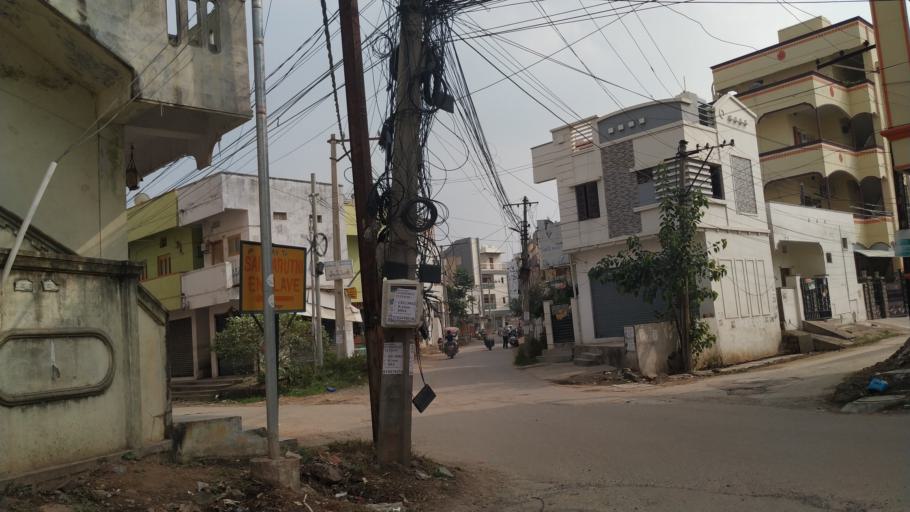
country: IN
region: Telangana
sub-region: Medak
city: Serilingampalle
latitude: 17.4921
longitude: 78.3191
